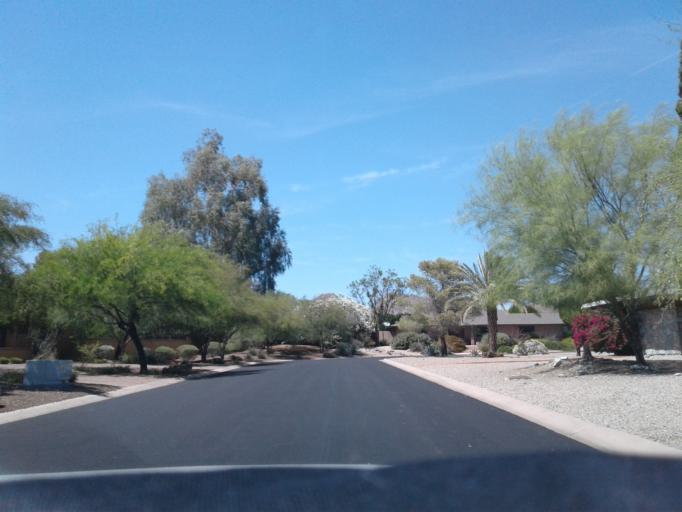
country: US
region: Arizona
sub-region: Maricopa County
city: Paradise Valley
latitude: 33.5159
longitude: -112.0002
